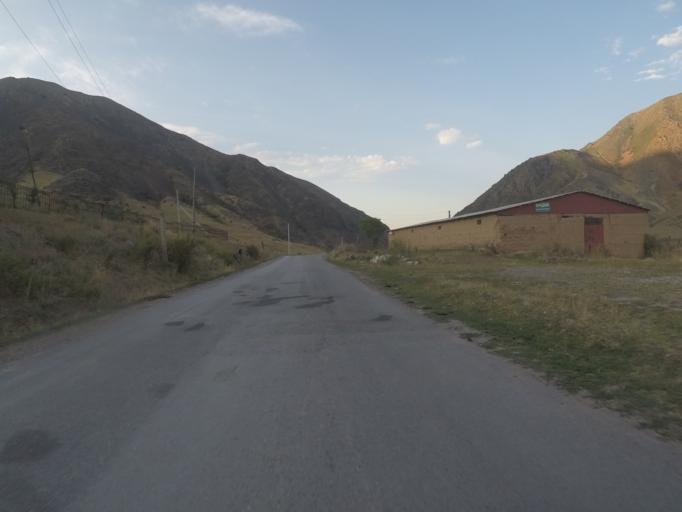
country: KG
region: Chuy
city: Bishkek
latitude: 42.6763
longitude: 74.6537
